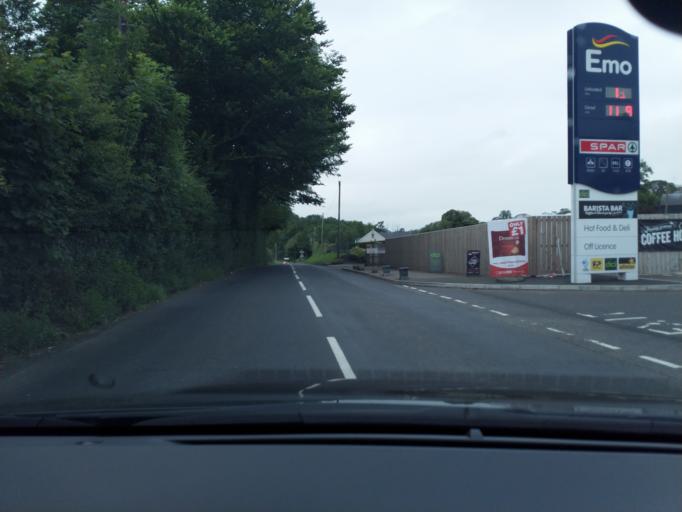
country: GB
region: Northern Ireland
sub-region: Dungannon District
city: Dungannon
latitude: 54.4455
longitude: -6.7952
